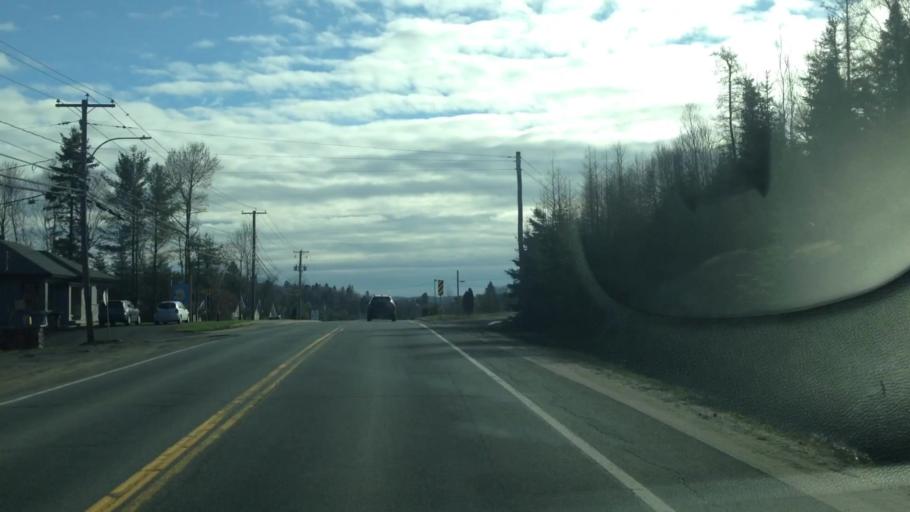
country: CA
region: Quebec
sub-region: Laurentides
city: Sainte-Adele
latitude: 46.0237
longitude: -74.0704
